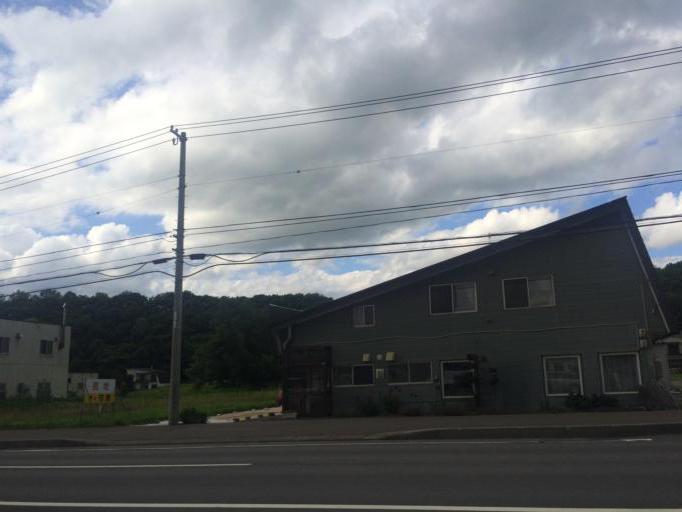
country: JP
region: Hokkaido
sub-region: Asahikawa-shi
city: Asahikawa
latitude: 43.7689
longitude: 142.2933
